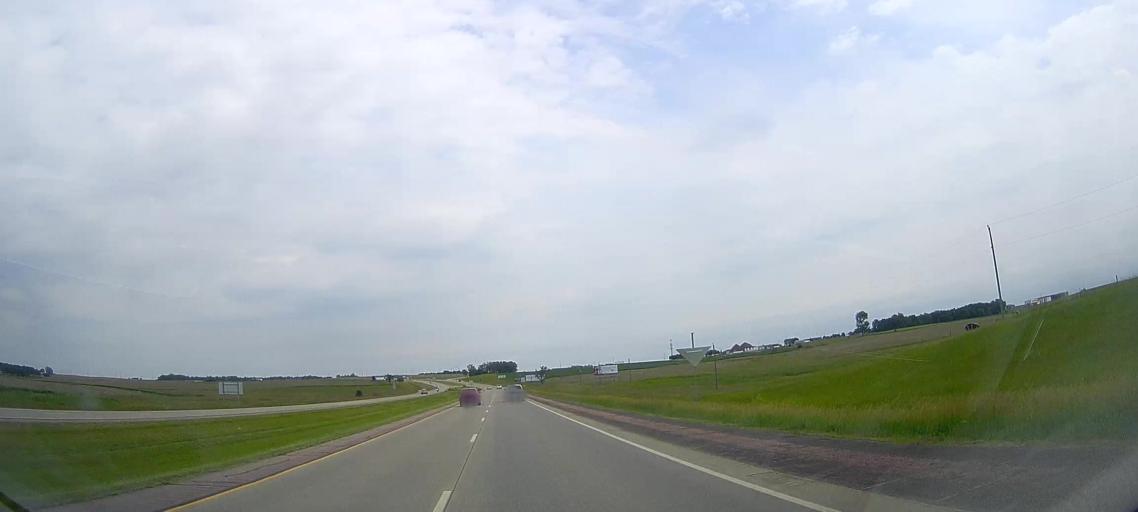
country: US
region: South Dakota
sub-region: Minnehaha County
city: Crooks
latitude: 43.6086
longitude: -96.8087
